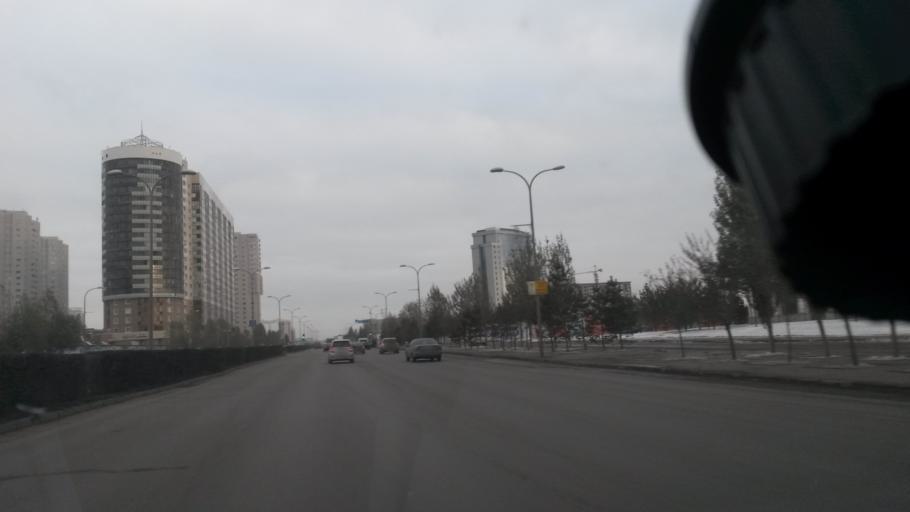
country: KZ
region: Astana Qalasy
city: Astana
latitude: 51.1187
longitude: 71.4572
